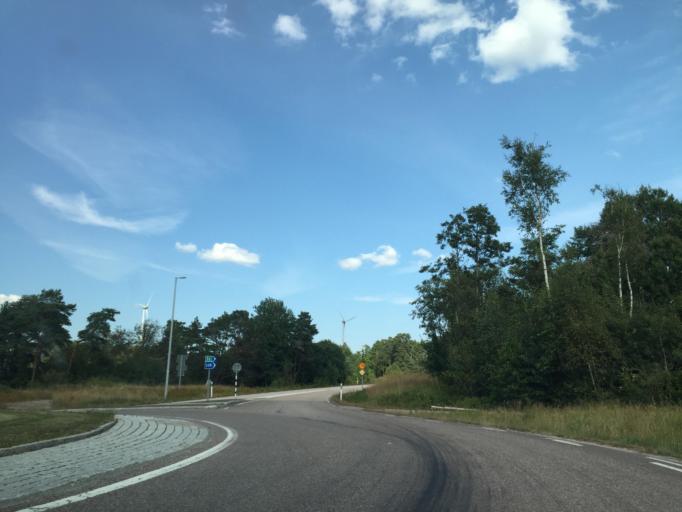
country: SE
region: Vaestra Goetaland
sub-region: Tanums Kommun
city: Tanumshede
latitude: 58.8111
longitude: 11.2643
